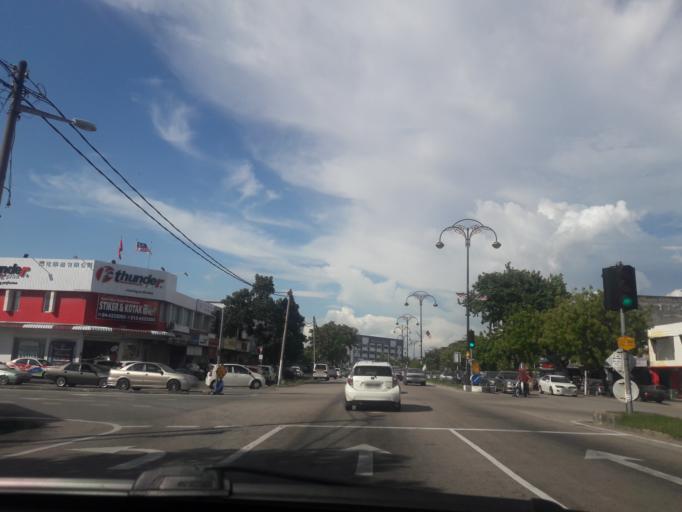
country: MY
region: Kedah
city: Sungai Petani
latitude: 5.6333
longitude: 100.4831
